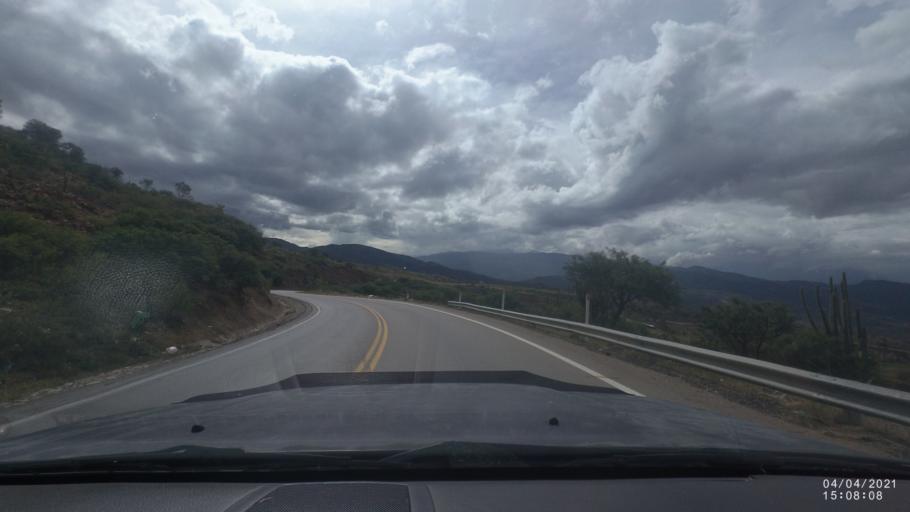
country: BO
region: Cochabamba
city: Capinota
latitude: -17.6034
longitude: -66.3560
